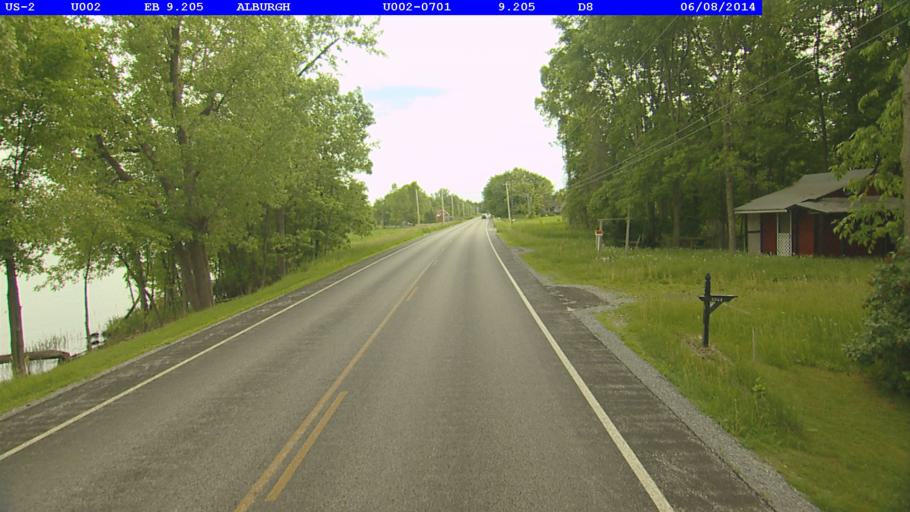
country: US
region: Vermont
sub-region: Grand Isle County
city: North Hero
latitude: 44.9181
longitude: -73.2759
